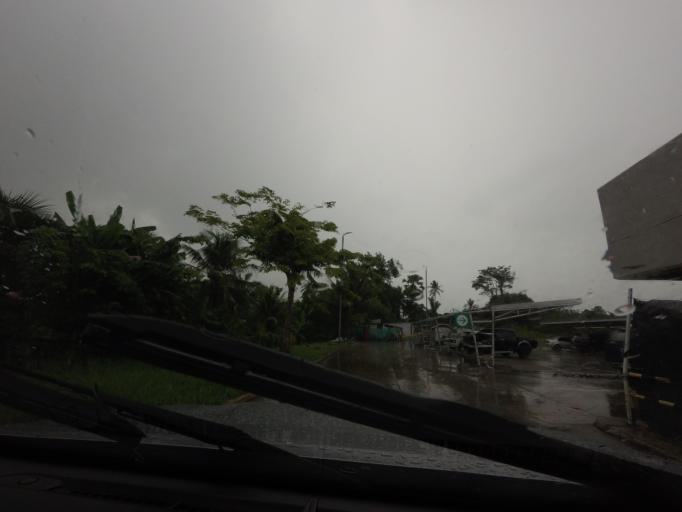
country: TH
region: Chumphon
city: Chumphon
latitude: 10.5044
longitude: 99.1381
